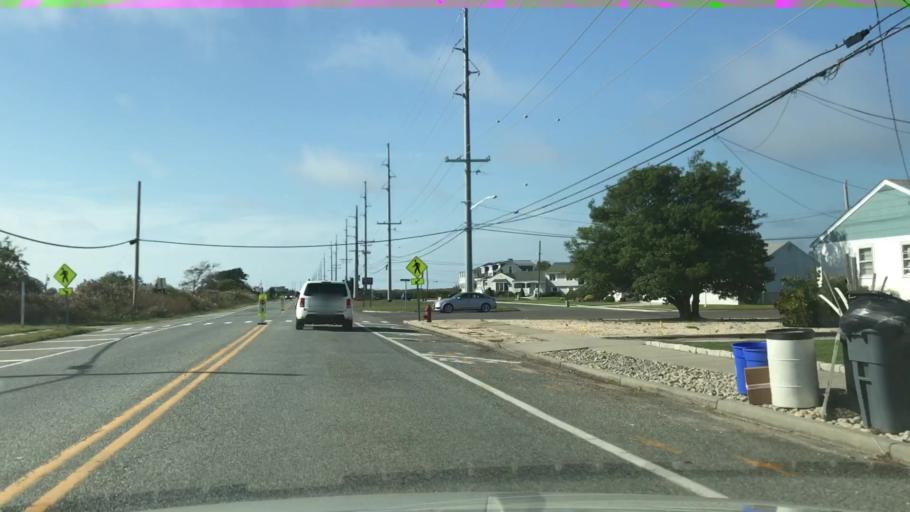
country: US
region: New Jersey
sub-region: Cape May County
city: Cape May Court House
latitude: 39.0597
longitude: -74.7700
